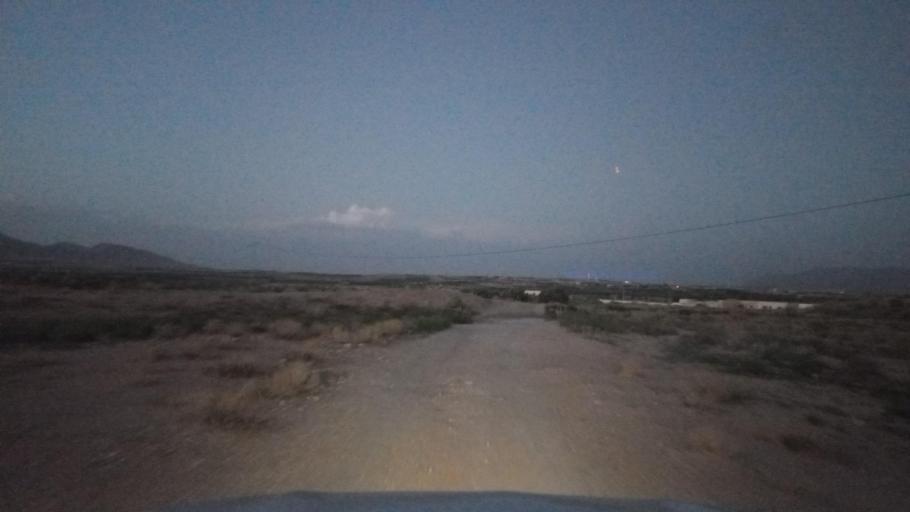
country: TN
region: Al Qasrayn
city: Sbiba
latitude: 35.3796
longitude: 9.0261
